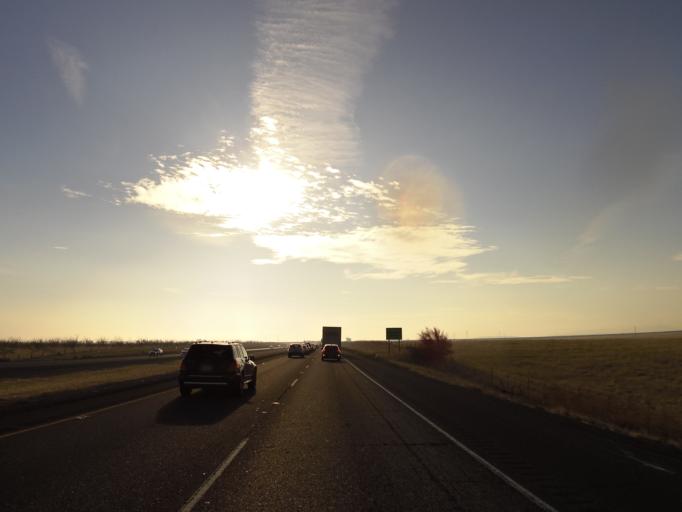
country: US
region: California
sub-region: Merced County
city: Los Banos
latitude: 37.0752
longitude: -120.9880
